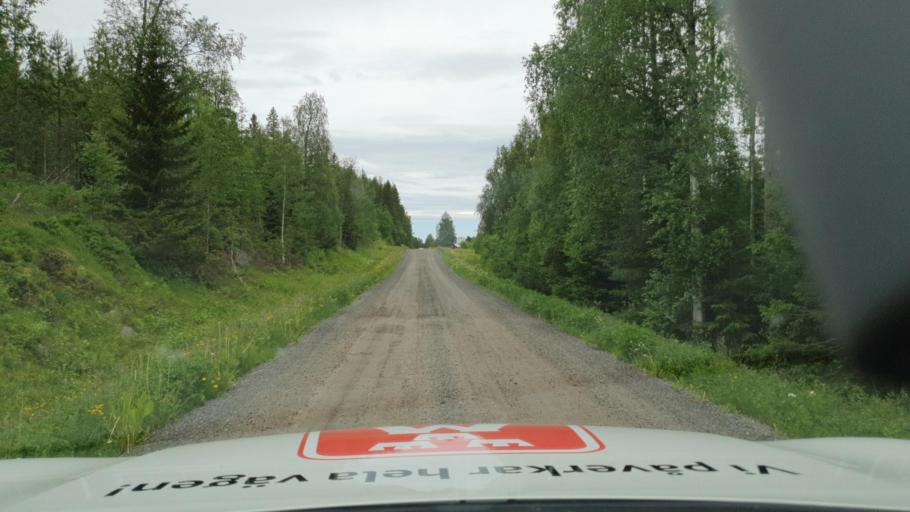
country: SE
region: Vaesterbotten
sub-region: Skelleftea Kommun
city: Burtraesk
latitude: 64.3902
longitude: 20.6096
